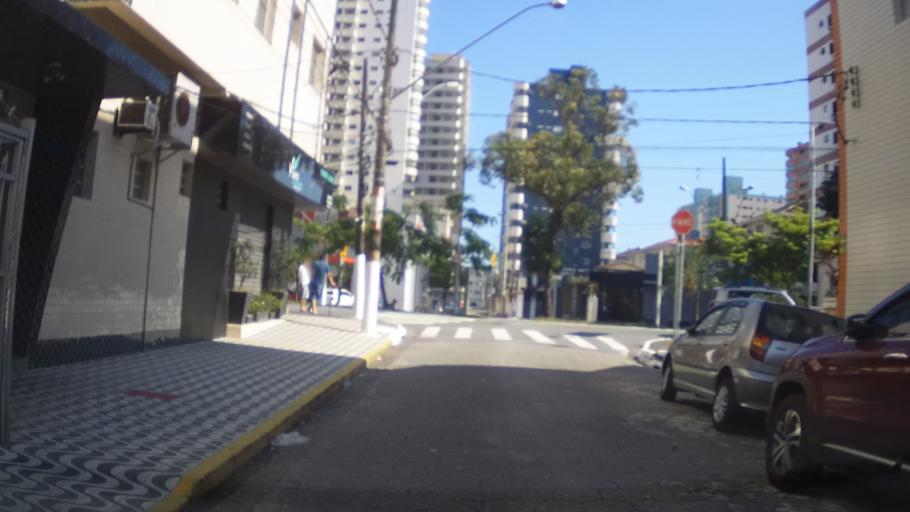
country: BR
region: Sao Paulo
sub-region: Praia Grande
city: Praia Grande
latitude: -24.0133
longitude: -46.4006
